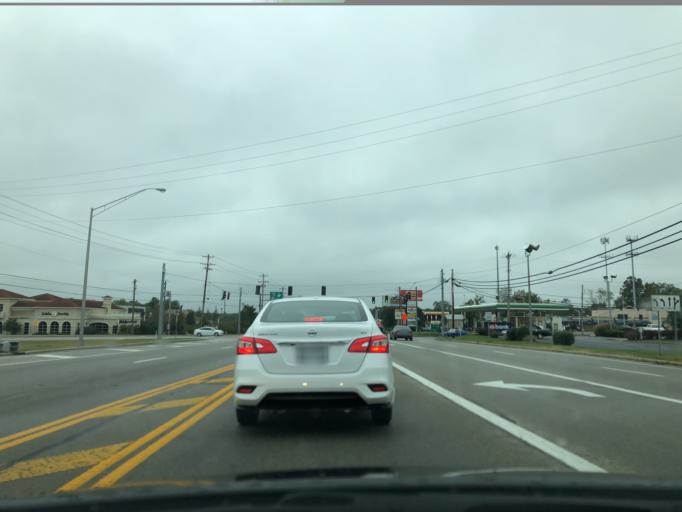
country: US
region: Ohio
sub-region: Hamilton County
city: Sixteen Mile Stand
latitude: 39.2606
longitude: -84.3388
